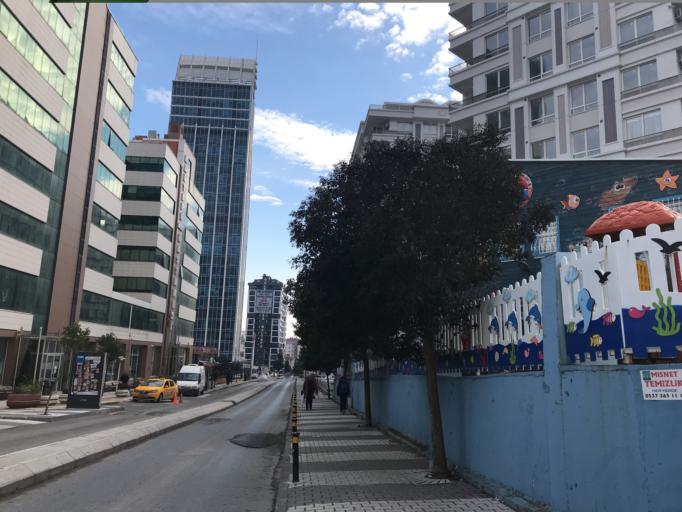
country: TR
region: Istanbul
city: Maltepe
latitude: 40.9373
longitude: 29.1351
